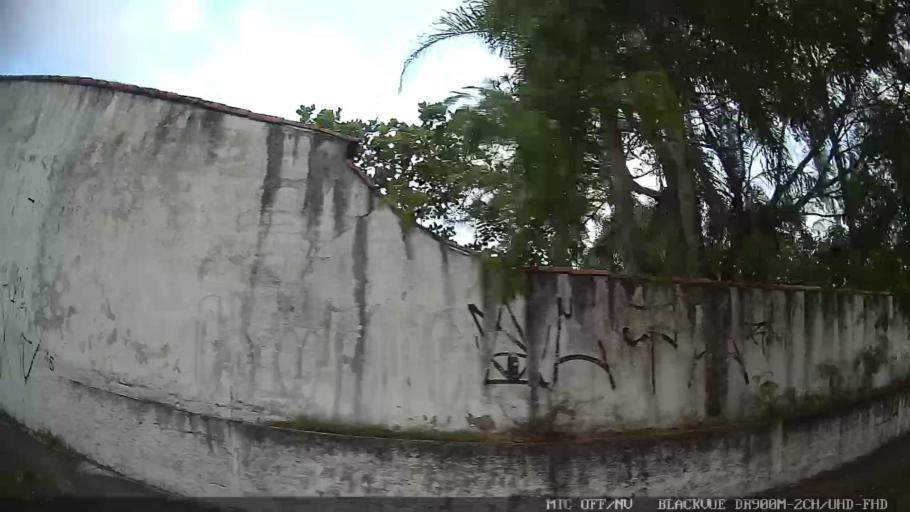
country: BR
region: Sao Paulo
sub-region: Peruibe
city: Peruibe
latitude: -24.3053
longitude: -46.9920
